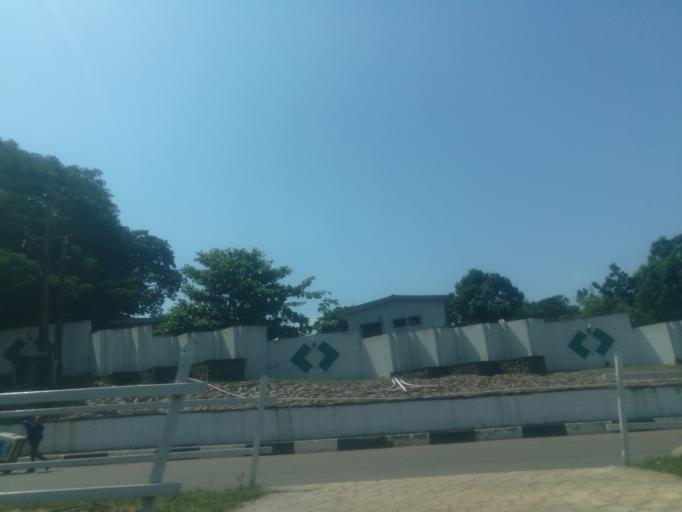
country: NG
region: Ogun
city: Abeokuta
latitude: 7.1441
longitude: 3.3416
